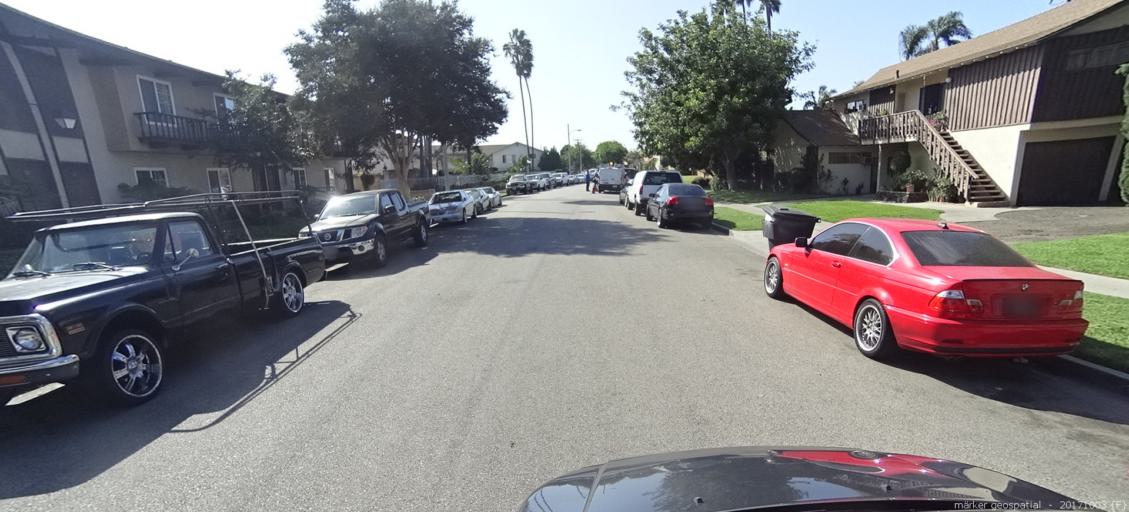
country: US
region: California
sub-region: Orange County
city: Garden Grove
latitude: 33.7758
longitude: -117.9601
